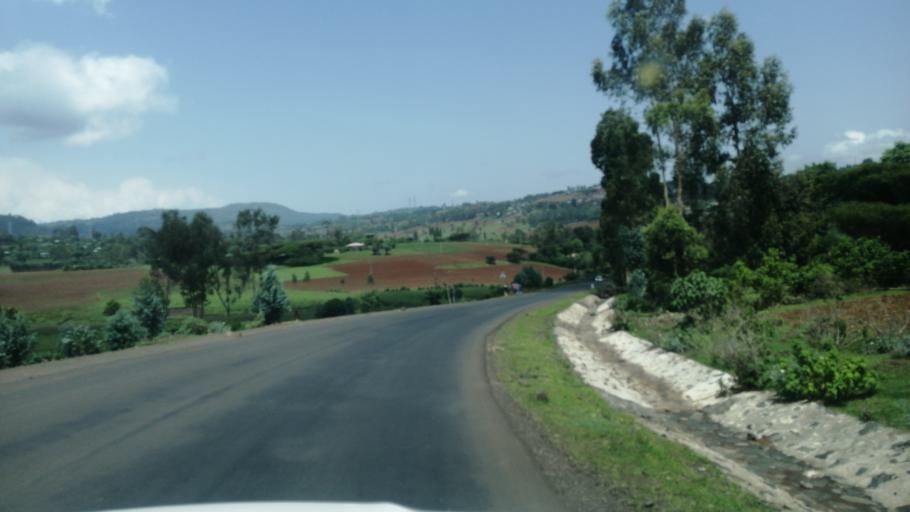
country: ET
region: Oromiya
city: Gedo
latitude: 8.9744
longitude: 37.5587
